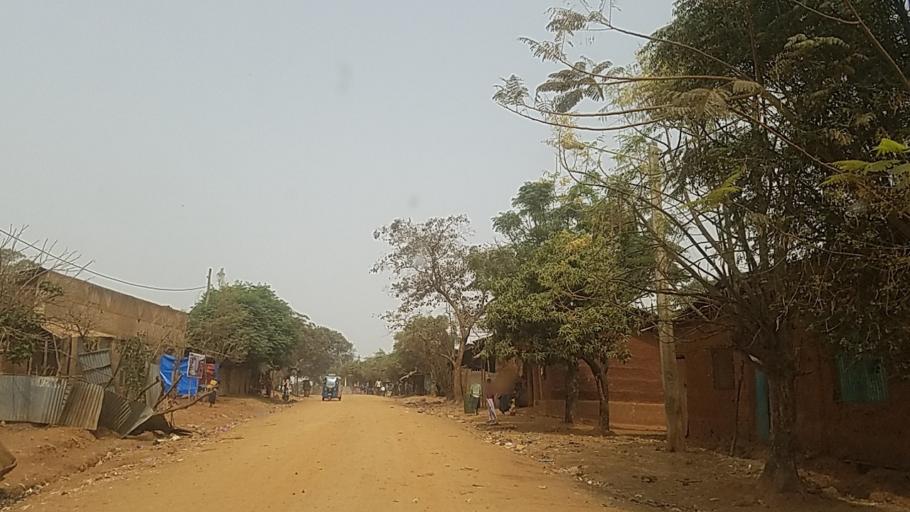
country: ET
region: Amhara
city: Bure
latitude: 10.7758
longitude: 36.2639
